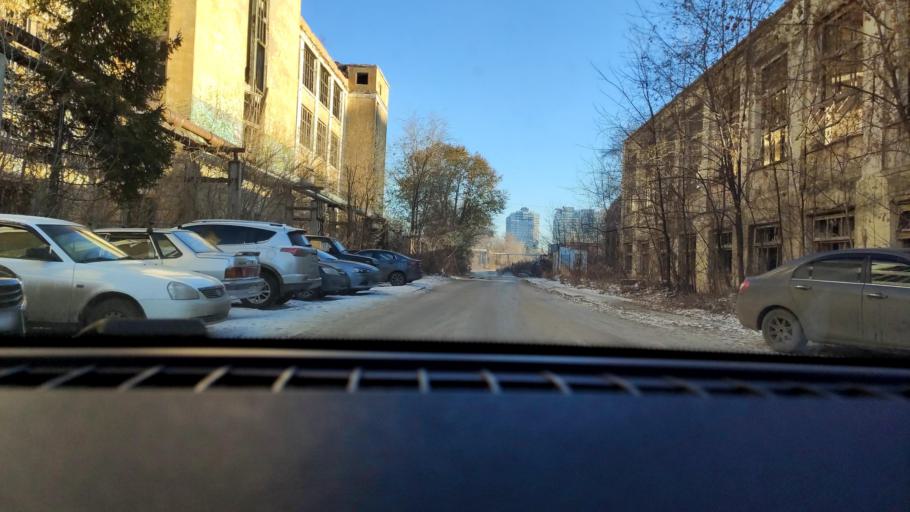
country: RU
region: Samara
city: Samara
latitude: 53.2174
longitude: 50.1418
